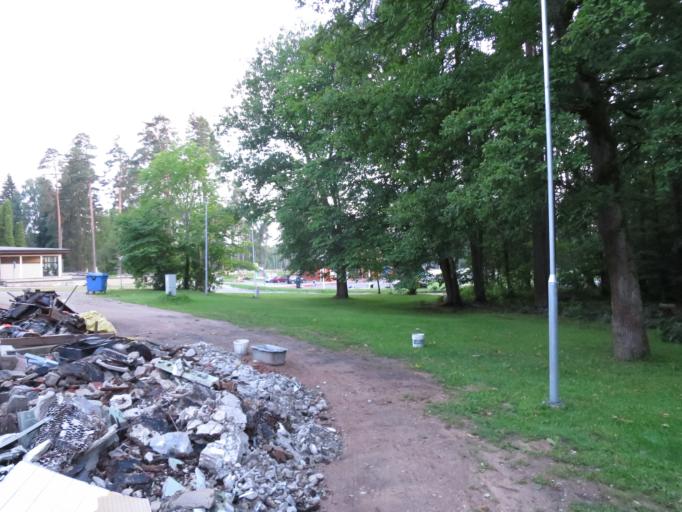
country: LV
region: Sigulda
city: Sigulda
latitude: 57.1410
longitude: 24.8180
